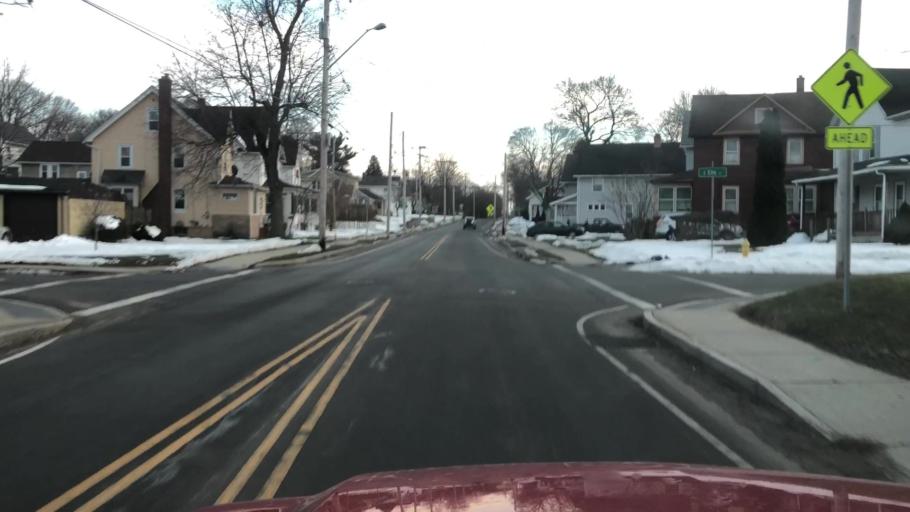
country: US
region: New York
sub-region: Monroe County
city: East Rochester
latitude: 43.1108
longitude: -77.4796
